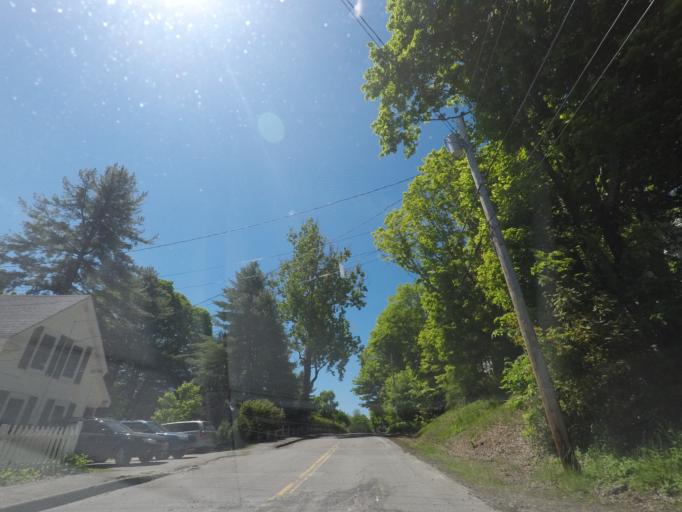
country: US
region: Maine
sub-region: Kennebec County
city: Hallowell
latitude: 44.2830
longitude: -69.7947
